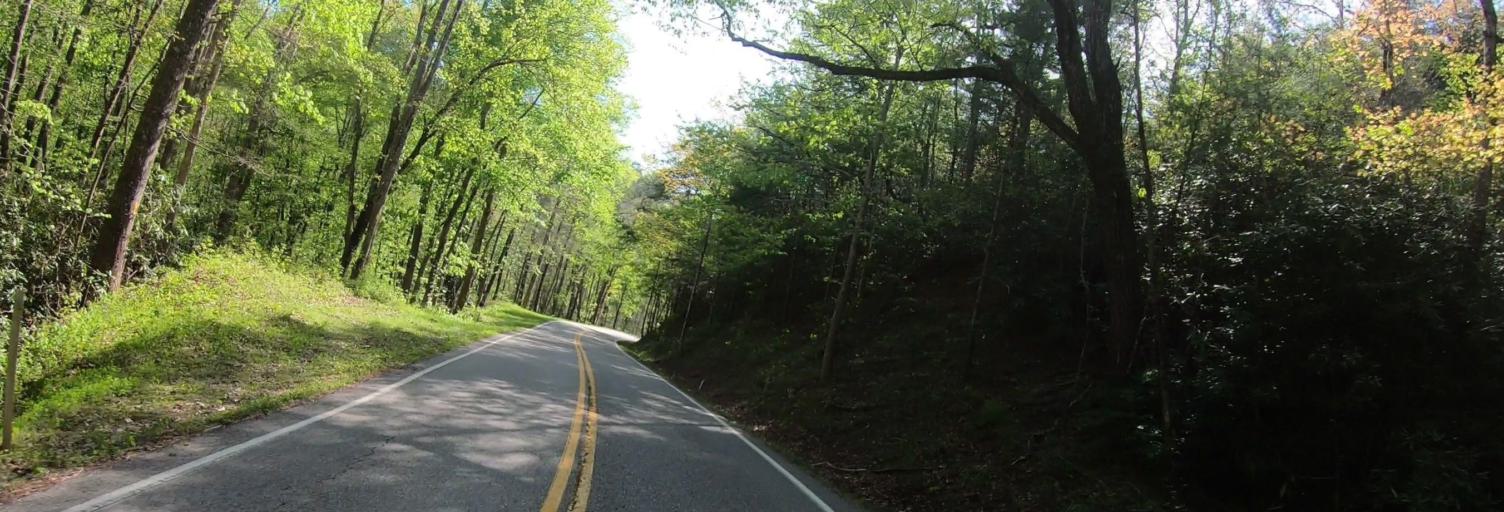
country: US
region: North Carolina
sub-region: Graham County
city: Robbinsville
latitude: 35.4972
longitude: -83.9282
